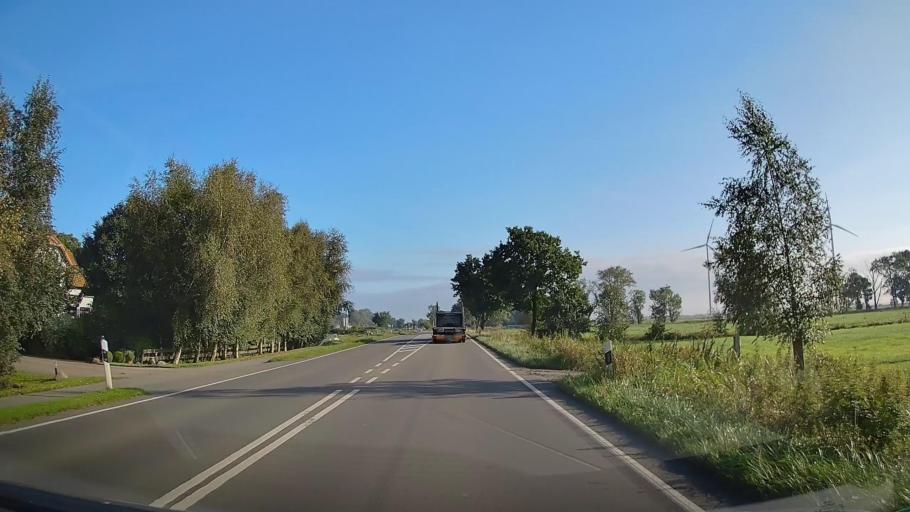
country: DE
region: Lower Saxony
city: Ovelgonne
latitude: 53.2799
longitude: 8.3676
